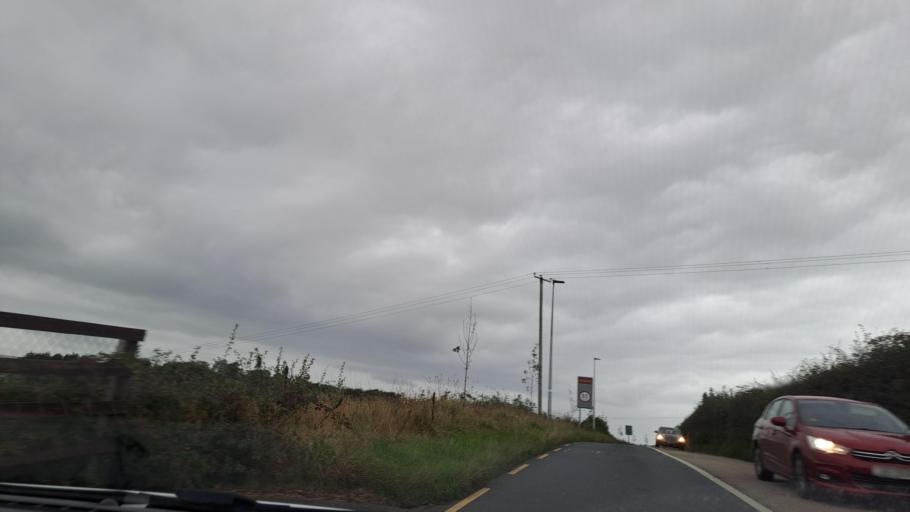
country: IE
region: Ulster
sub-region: An Cabhan
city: Bailieborough
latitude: 53.9981
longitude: -6.8987
